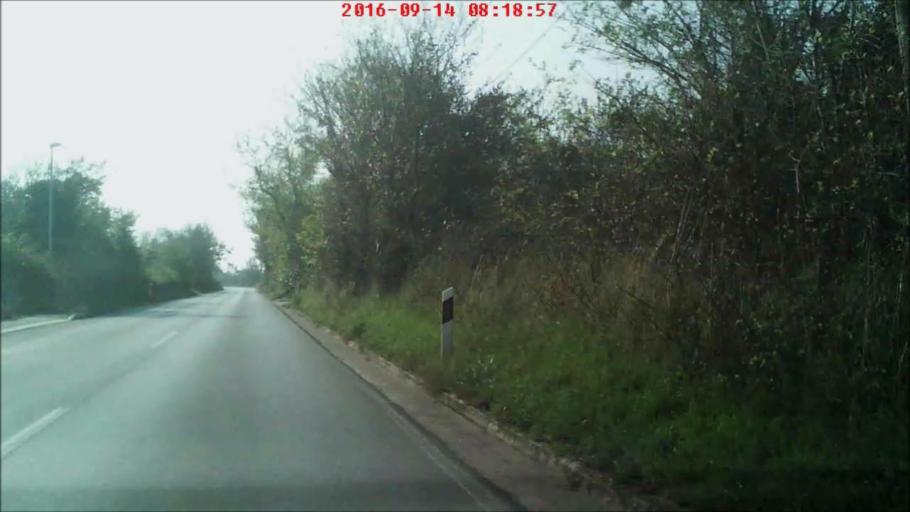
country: HR
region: Zadarska
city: Nin
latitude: 44.2360
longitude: 15.1864
